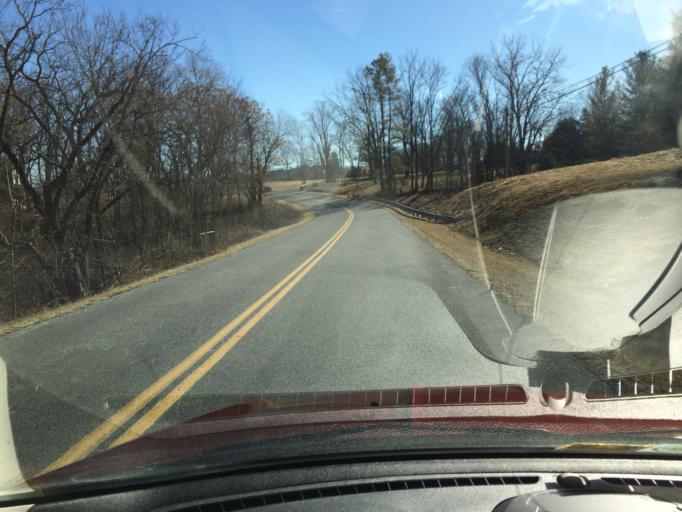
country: US
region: Virginia
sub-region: Rockingham County
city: Bridgewater
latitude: 38.3677
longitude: -78.9767
